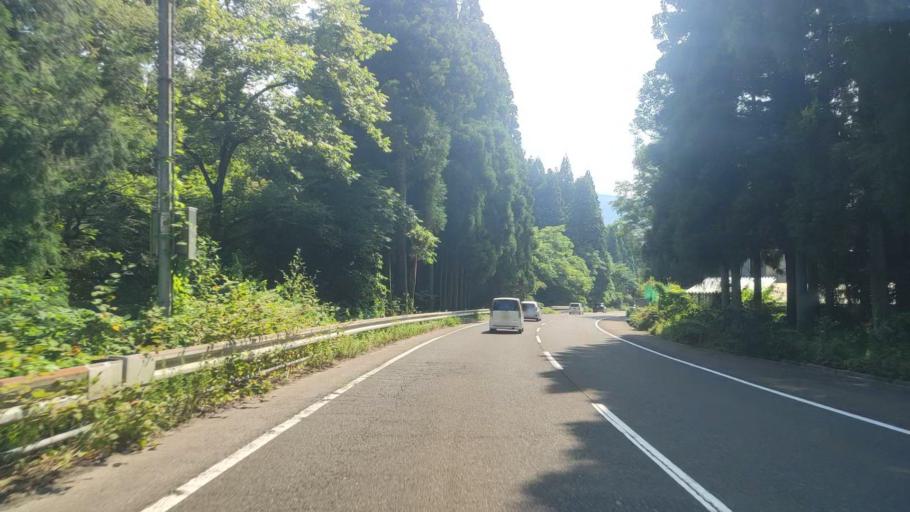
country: JP
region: Fukui
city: Tsuruga
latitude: 35.6058
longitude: 136.1121
